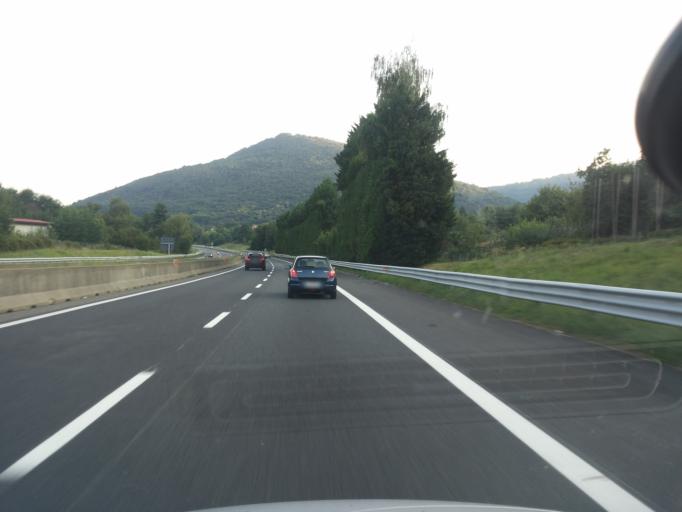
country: IT
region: Piedmont
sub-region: Provincia Verbano-Cusio-Ossola
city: Brovello
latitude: 45.8507
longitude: 8.5341
